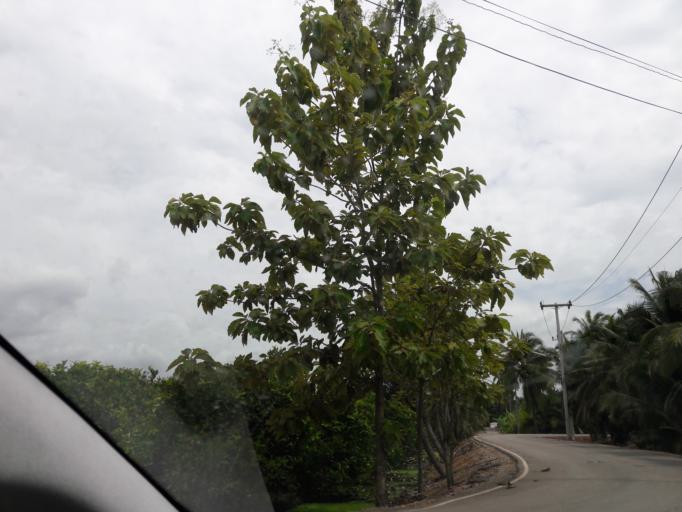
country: TH
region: Ratchaburi
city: Damnoen Saduak
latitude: 13.5336
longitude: 99.9518
